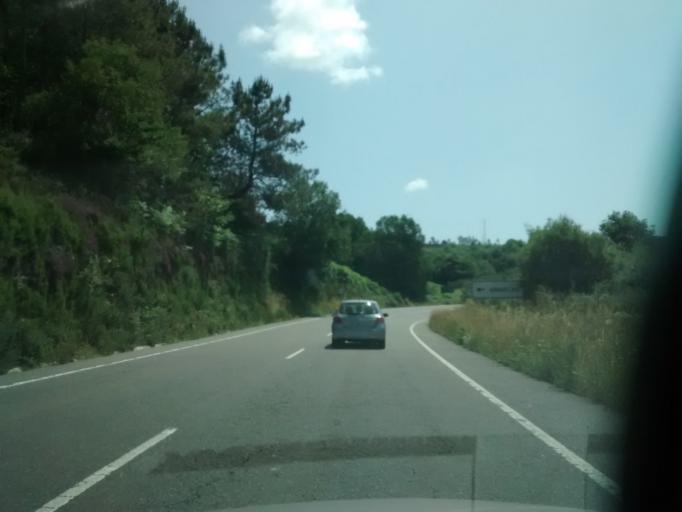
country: ES
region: Galicia
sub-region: Provincia de Pontevedra
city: Forcarei
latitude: 42.5164
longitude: -8.2649
